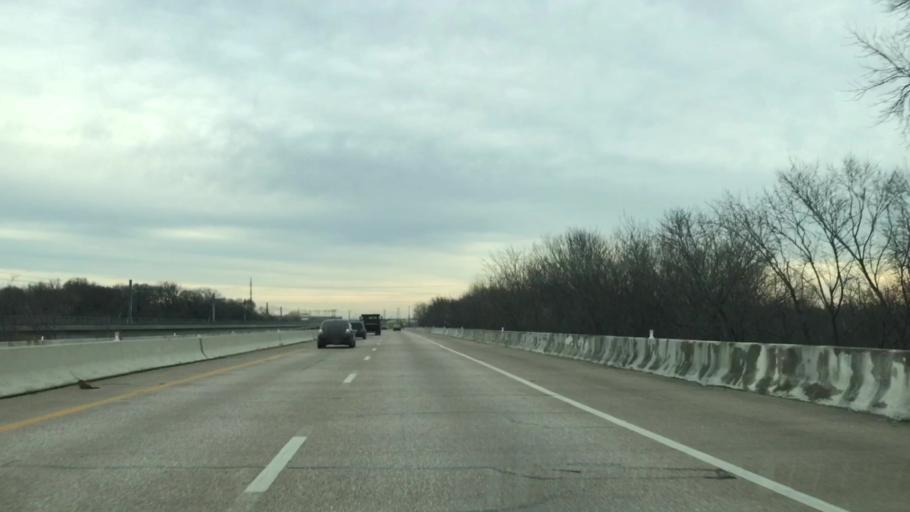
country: US
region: Texas
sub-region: Dallas County
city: Irving
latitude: 32.8482
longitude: -96.8927
